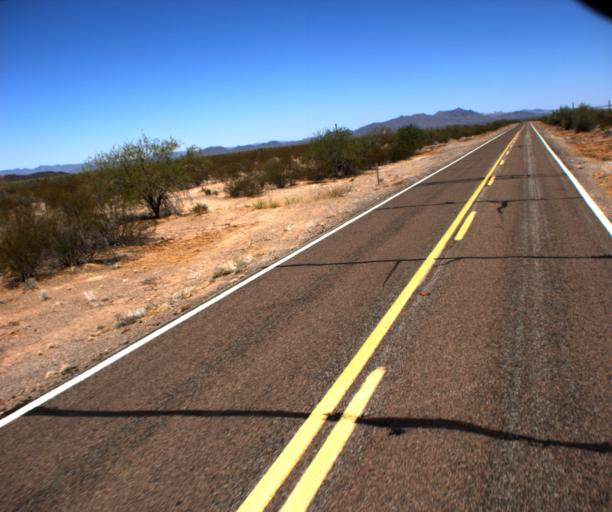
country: US
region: Arizona
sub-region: Pima County
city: Ajo
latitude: 32.2353
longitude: -112.7177
